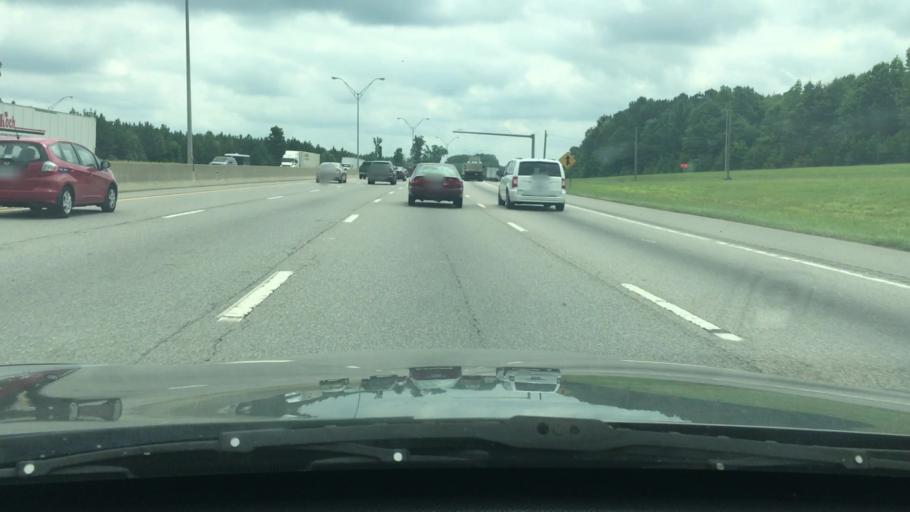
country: US
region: North Carolina
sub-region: Alamance County
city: Mebane
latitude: 36.0792
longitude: -79.2240
